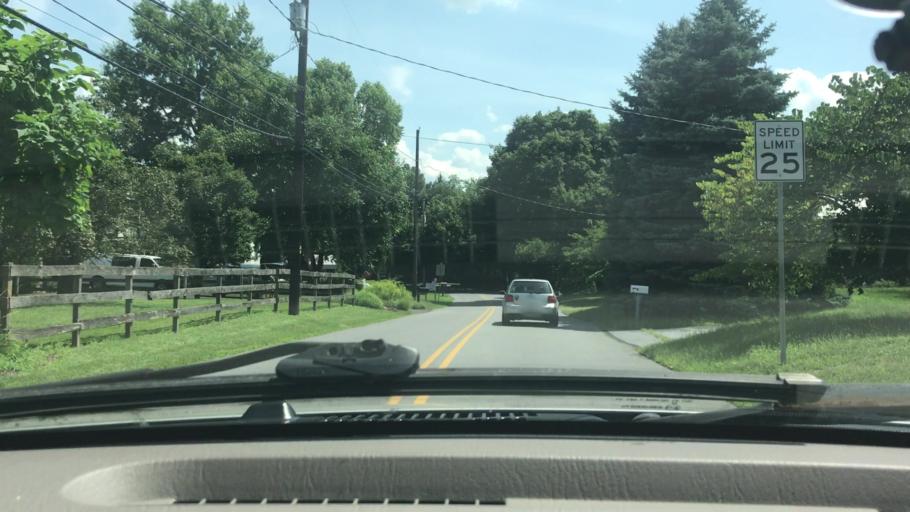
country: US
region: Pennsylvania
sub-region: Dauphin County
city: Rutherford
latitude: 40.2570
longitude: -76.7474
